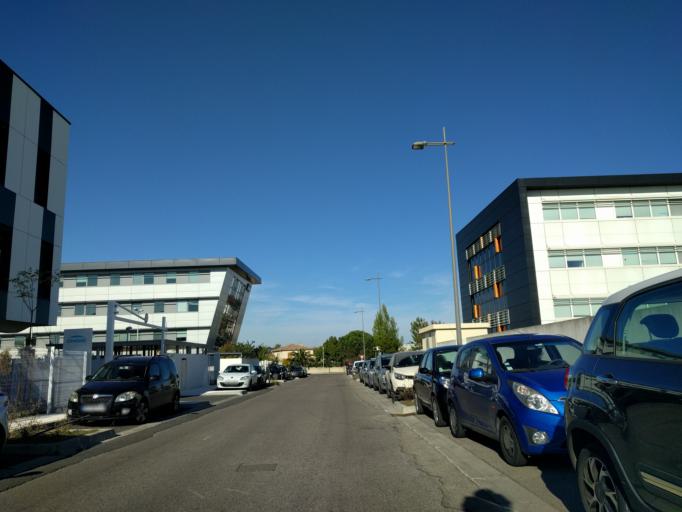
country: FR
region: Languedoc-Roussillon
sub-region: Departement de l'Herault
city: Castelnau-le-Lez
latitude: 43.6210
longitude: 3.9091
